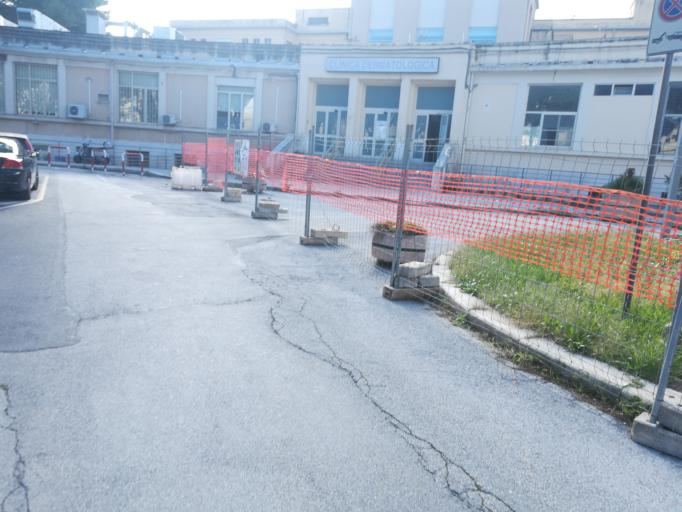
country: IT
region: Apulia
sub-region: Provincia di Bari
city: Bari
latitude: 41.1112
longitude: 16.8584
